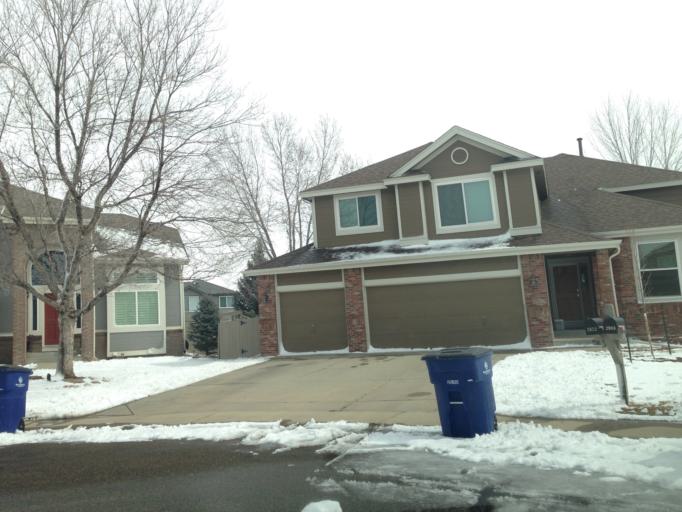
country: US
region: Colorado
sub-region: Boulder County
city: Lafayette
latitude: 39.9667
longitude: -105.0925
